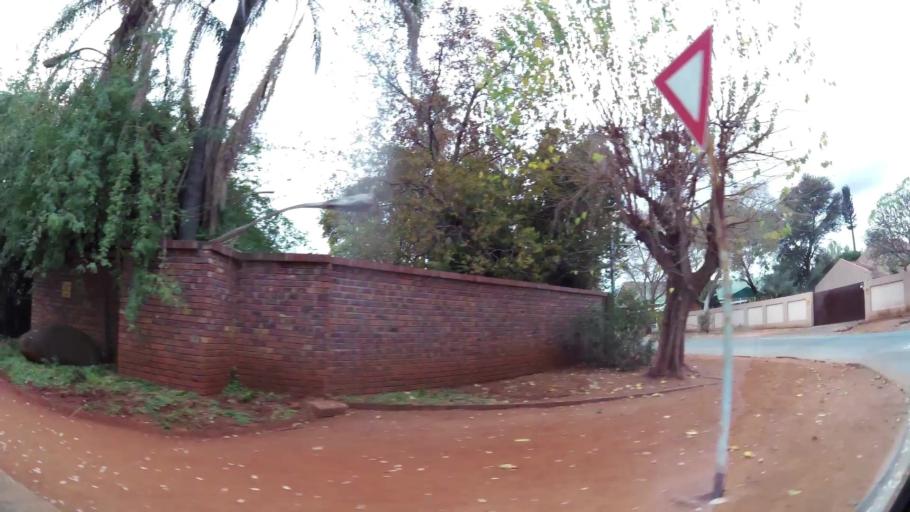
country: ZA
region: Limpopo
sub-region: Waterberg District Municipality
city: Mokopane
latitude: -24.1909
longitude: 28.9957
